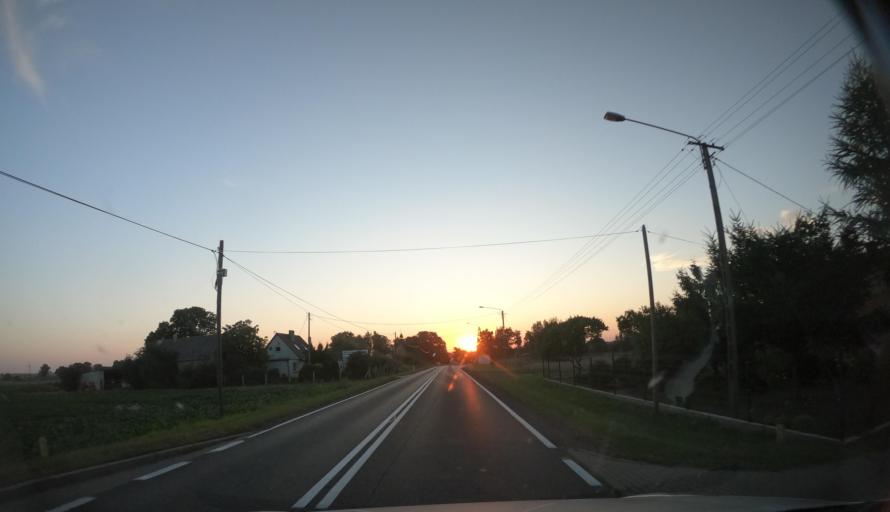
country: PL
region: Kujawsko-Pomorskie
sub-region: Powiat bydgoski
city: Koronowo
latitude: 53.3437
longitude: 17.8660
